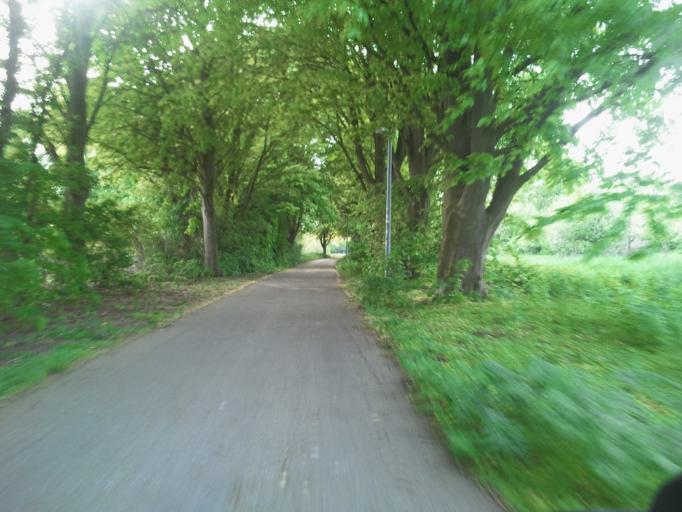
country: DE
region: Lower Saxony
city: Nienburg
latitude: 52.6320
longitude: 9.2338
